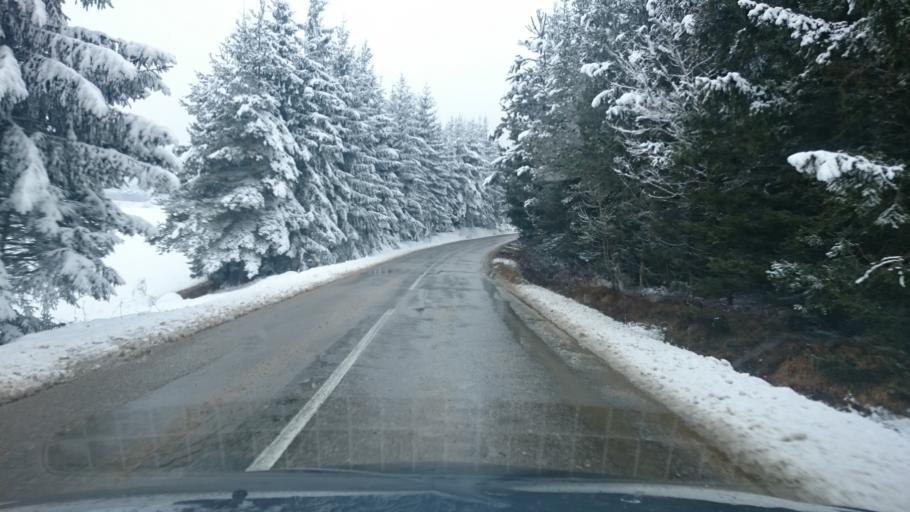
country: BA
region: Republika Srpska
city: Skender Vakuf
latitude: 44.4961
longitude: 17.3312
